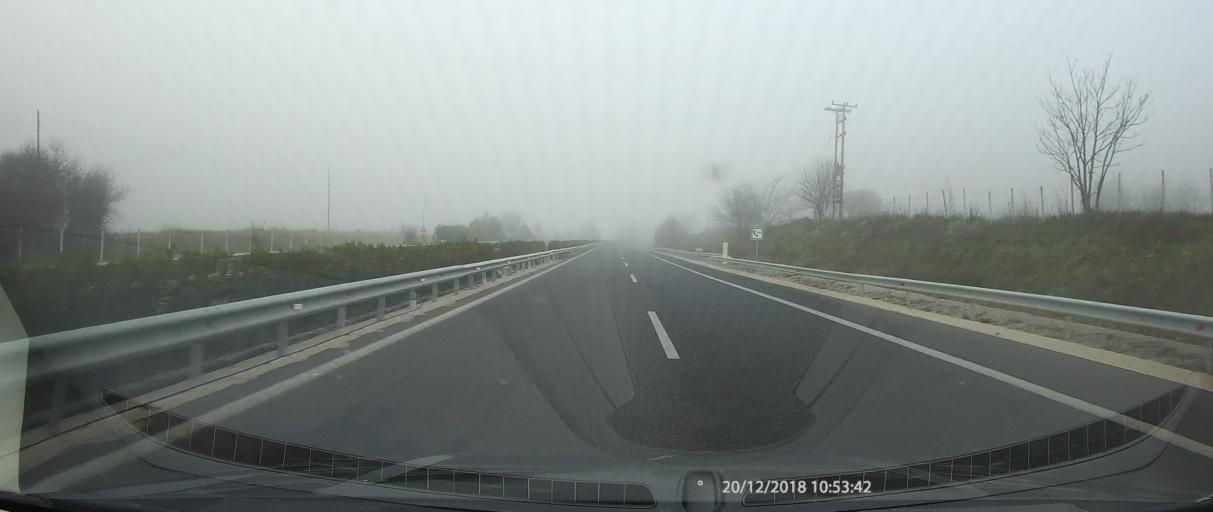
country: GR
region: Peloponnese
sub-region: Nomos Arkadias
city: Tripoli
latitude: 37.6128
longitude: 22.4578
